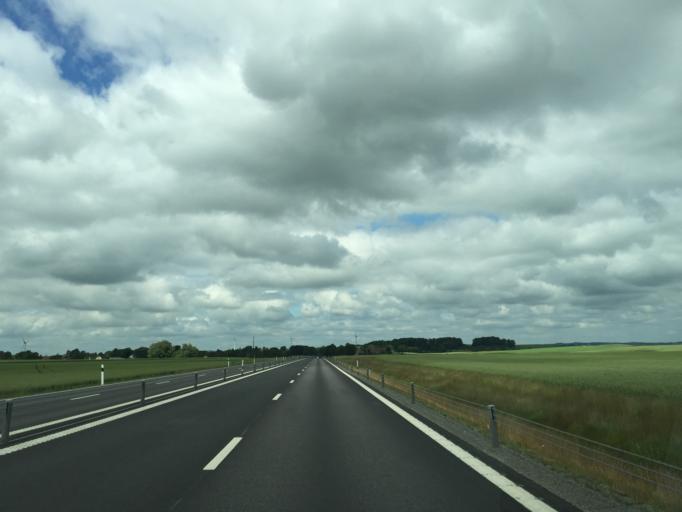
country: SE
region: Skane
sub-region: Svedala Kommun
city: Klagerup
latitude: 55.5865
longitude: 13.2555
